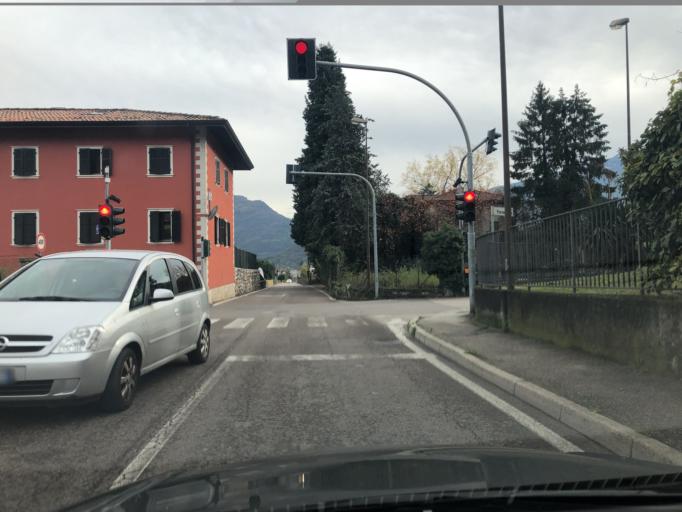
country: IT
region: Trentino-Alto Adige
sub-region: Provincia di Trento
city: Tenno
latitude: 45.9080
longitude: 10.8462
